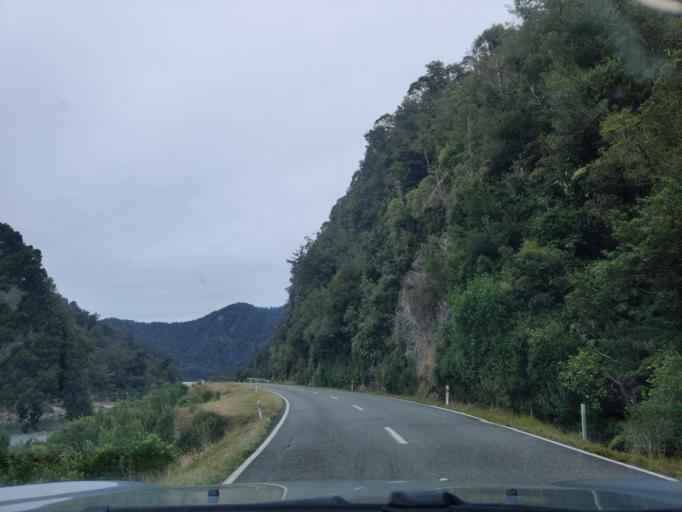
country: NZ
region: West Coast
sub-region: Buller District
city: Westport
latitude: -41.8570
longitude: 171.7593
